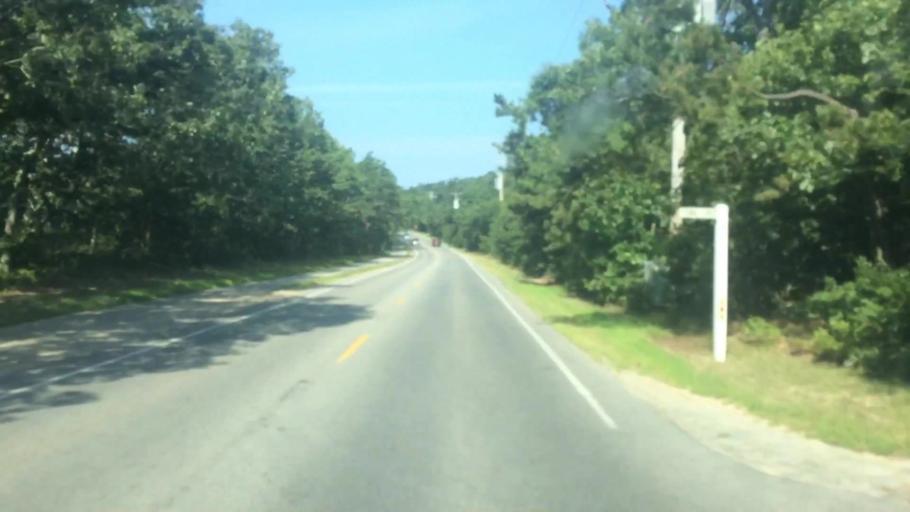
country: US
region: Massachusetts
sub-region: Dukes County
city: Oak Bluffs
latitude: 41.4136
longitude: -70.5778
